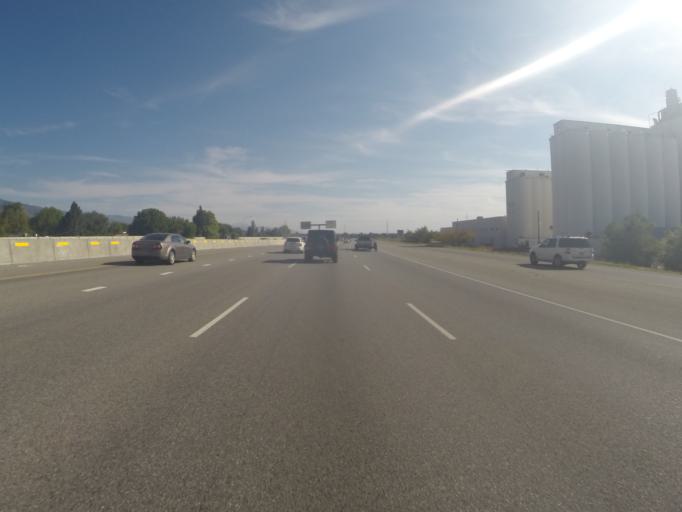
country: US
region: Utah
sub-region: Davis County
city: Kaysville
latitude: 41.0352
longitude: -111.9479
